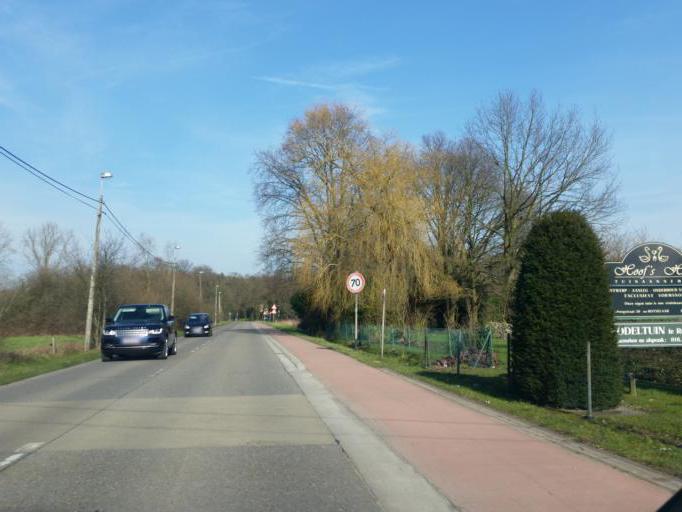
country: BE
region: Flanders
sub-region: Provincie Vlaams-Brabant
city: Boortmeerbeek
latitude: 50.9943
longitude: 4.5859
